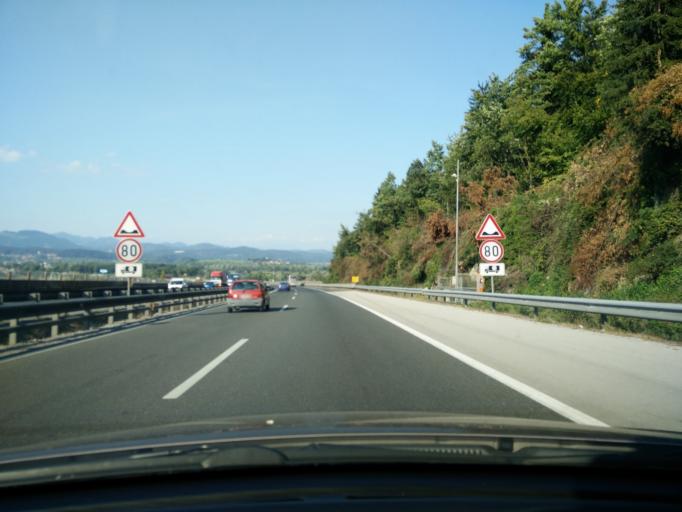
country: SI
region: Vrhnika
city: Verd
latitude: 45.9521
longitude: 14.3033
